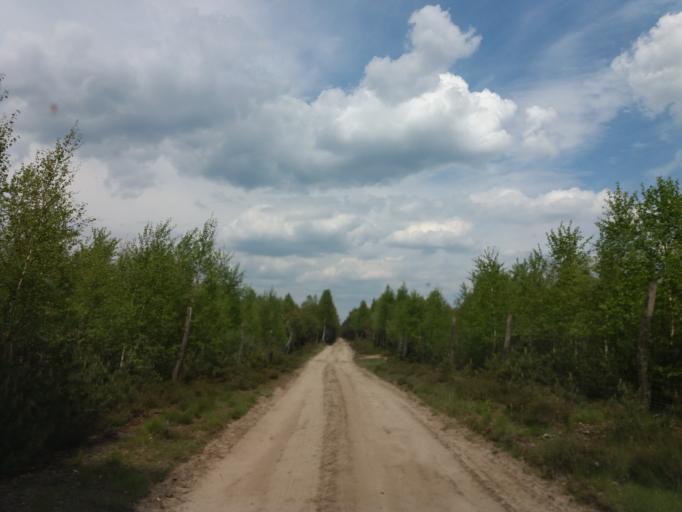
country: PL
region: West Pomeranian Voivodeship
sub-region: Powiat choszczenski
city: Drawno
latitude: 53.1758
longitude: 15.7565
